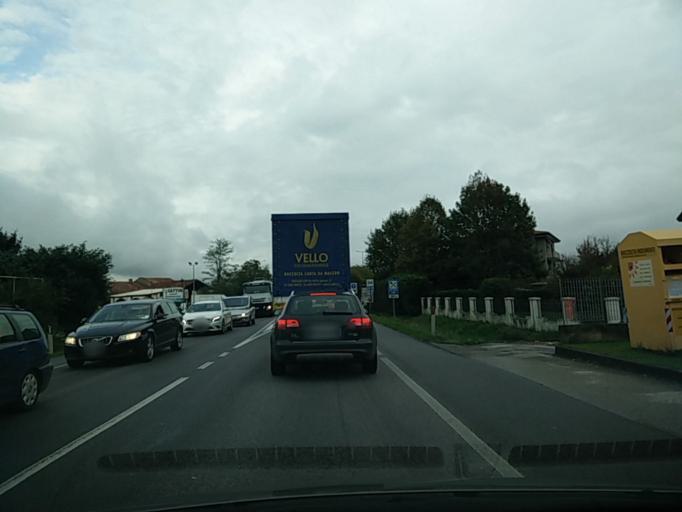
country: IT
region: Veneto
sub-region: Provincia di Treviso
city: Castelfranco Veneto
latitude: 45.6801
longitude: 11.9182
